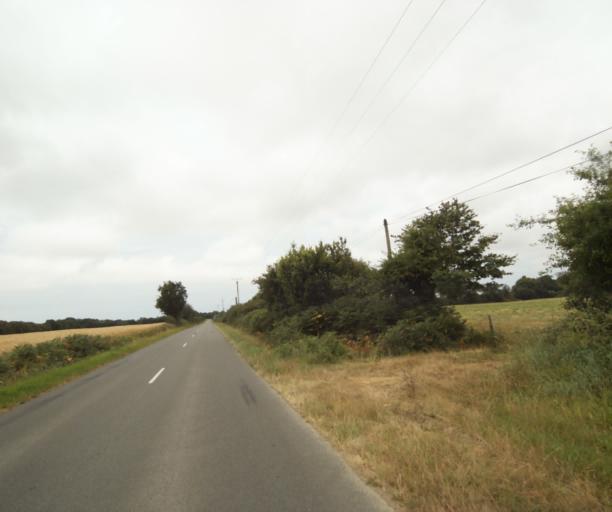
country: FR
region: Pays de la Loire
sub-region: Departement de la Vendee
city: Chateau-d'Olonne
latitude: 46.4996
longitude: -1.6953
